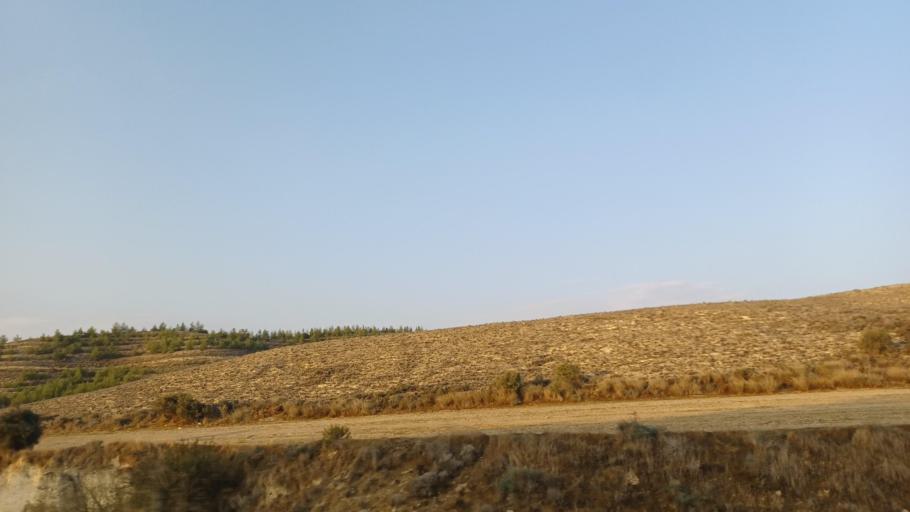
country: CY
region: Larnaka
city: Athienou
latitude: 35.0043
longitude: 33.5247
